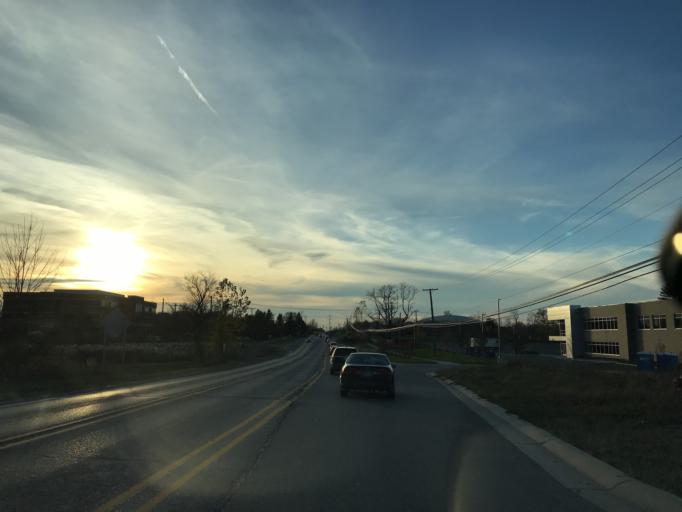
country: US
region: Michigan
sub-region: Oakland County
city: Novi
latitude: 42.4949
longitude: -83.5015
